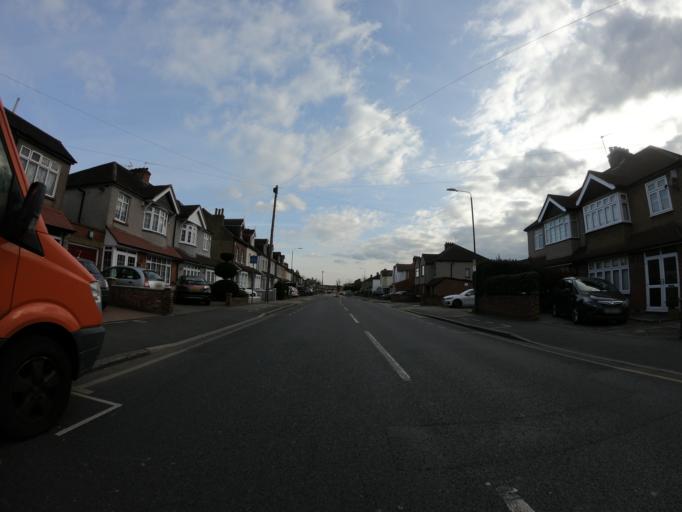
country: GB
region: England
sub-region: Greater London
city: Bexleyheath
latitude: 51.4653
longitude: 0.1404
